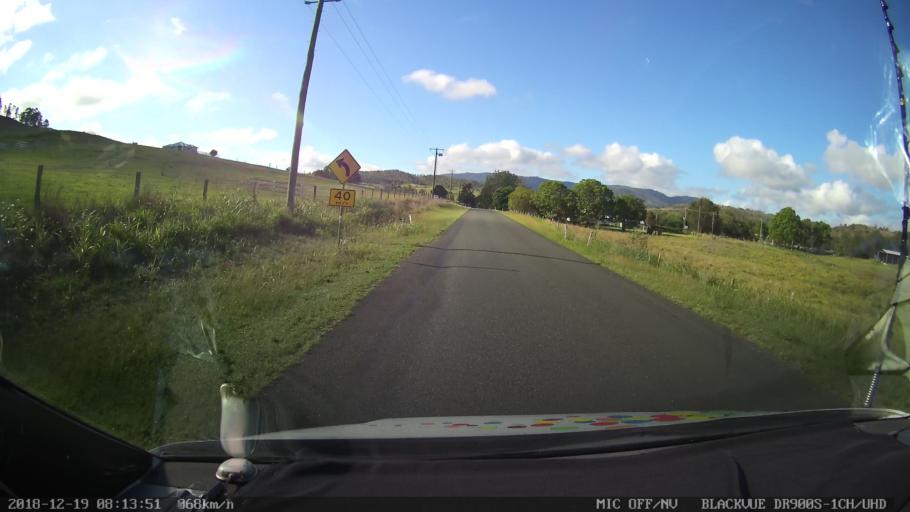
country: AU
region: Queensland
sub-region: Logan
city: Cedar Vale
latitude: -28.2428
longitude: 152.8901
